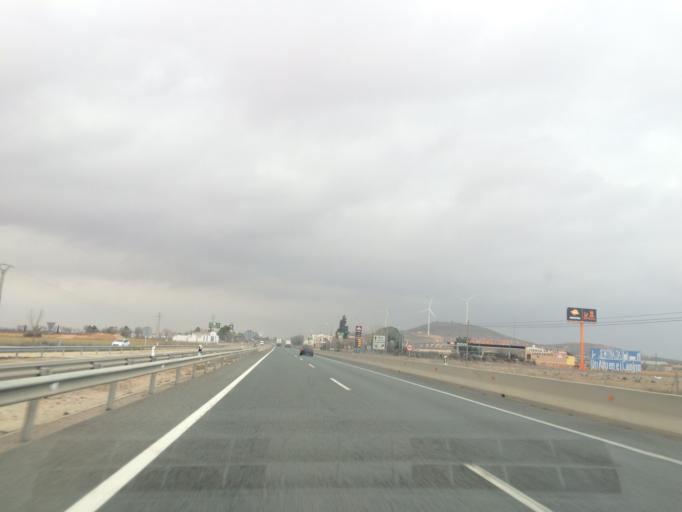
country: ES
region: Castille-La Mancha
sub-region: Province of Toledo
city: Madridejos
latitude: 39.5142
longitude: -3.5245
